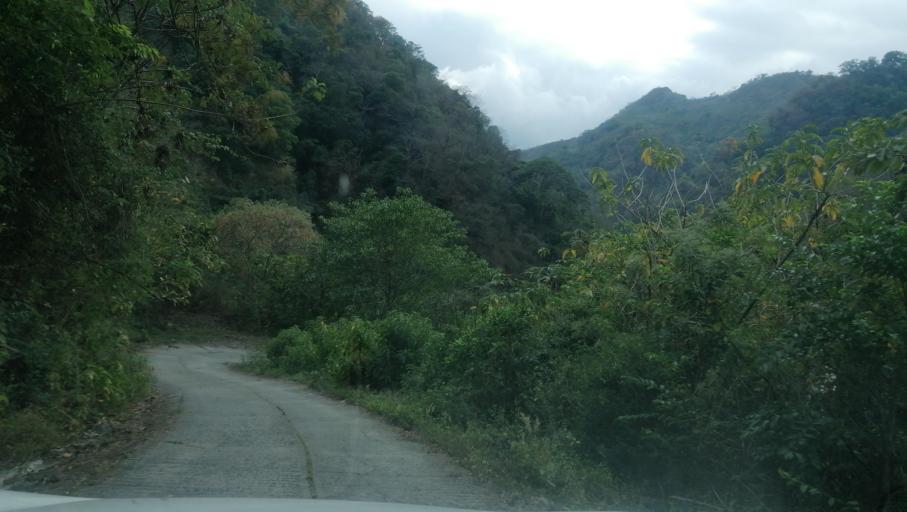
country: MX
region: Chiapas
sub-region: Cacahoatan
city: Benito Juarez
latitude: 15.1574
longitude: -92.1802
